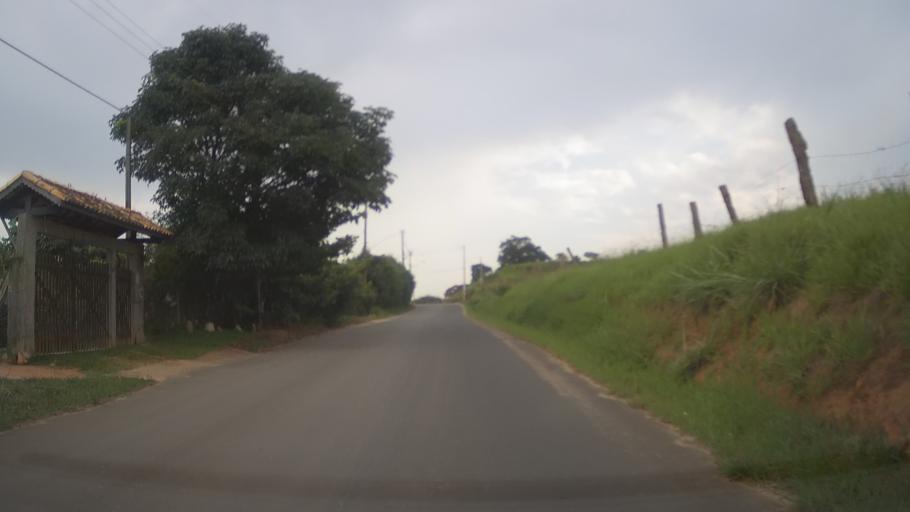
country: BR
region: Sao Paulo
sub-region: Itupeva
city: Itupeva
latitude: -23.1789
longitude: -47.0896
